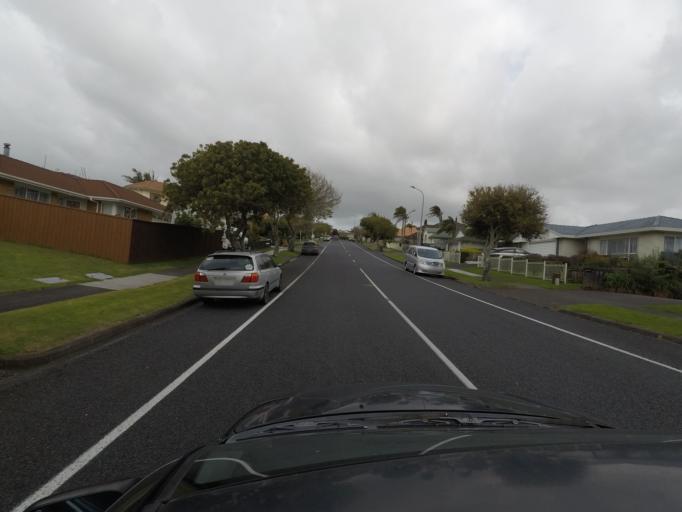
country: NZ
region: Auckland
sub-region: Auckland
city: Pakuranga
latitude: -36.9225
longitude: 174.9203
